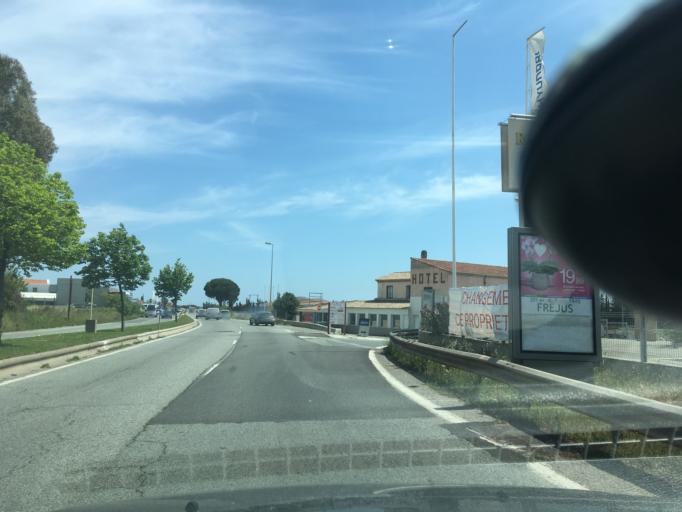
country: FR
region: Provence-Alpes-Cote d'Azur
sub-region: Departement du Var
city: Puget-sur-Argens
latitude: 43.4512
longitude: 6.6922
